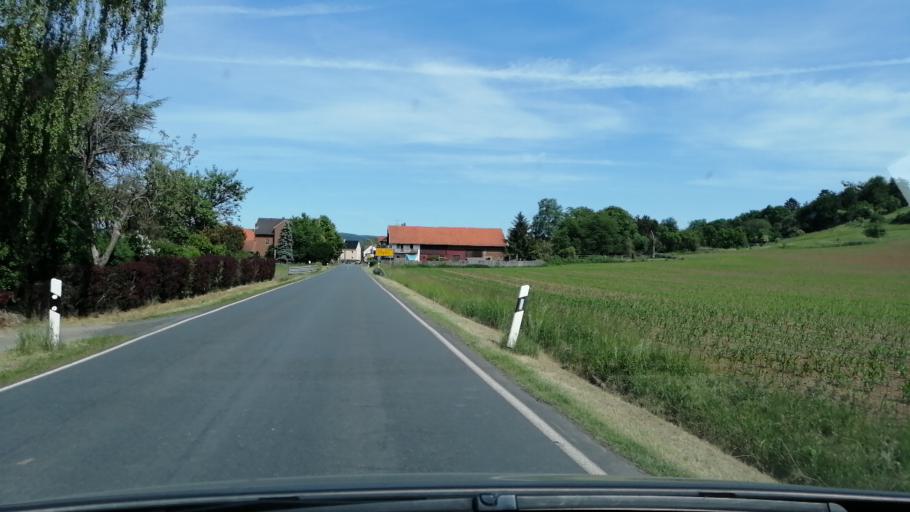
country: DE
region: Hesse
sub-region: Regierungsbezirk Kassel
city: Bad Wildungen
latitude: 51.1640
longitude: 9.0994
